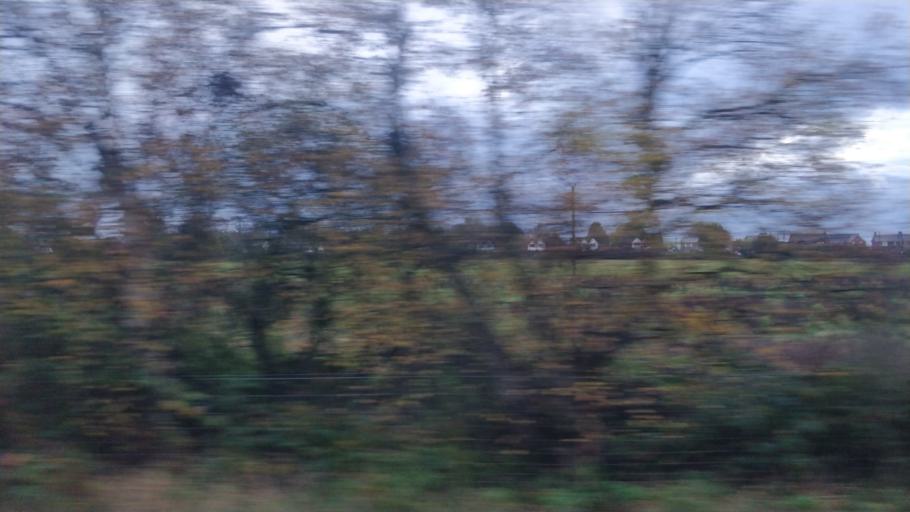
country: GB
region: England
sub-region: Lancashire
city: Banks
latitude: 53.6246
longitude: -2.9172
